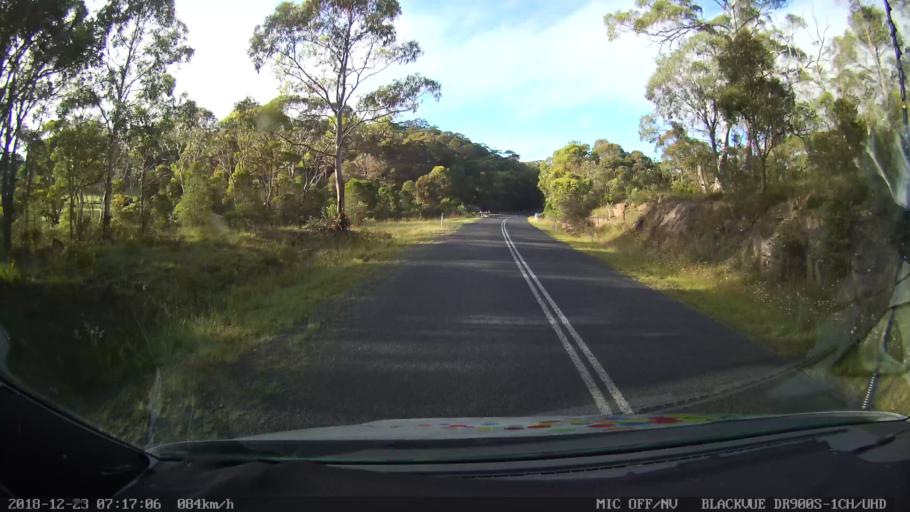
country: AU
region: New South Wales
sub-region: Bellingen
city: Dorrigo
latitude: -30.4643
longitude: 152.3071
